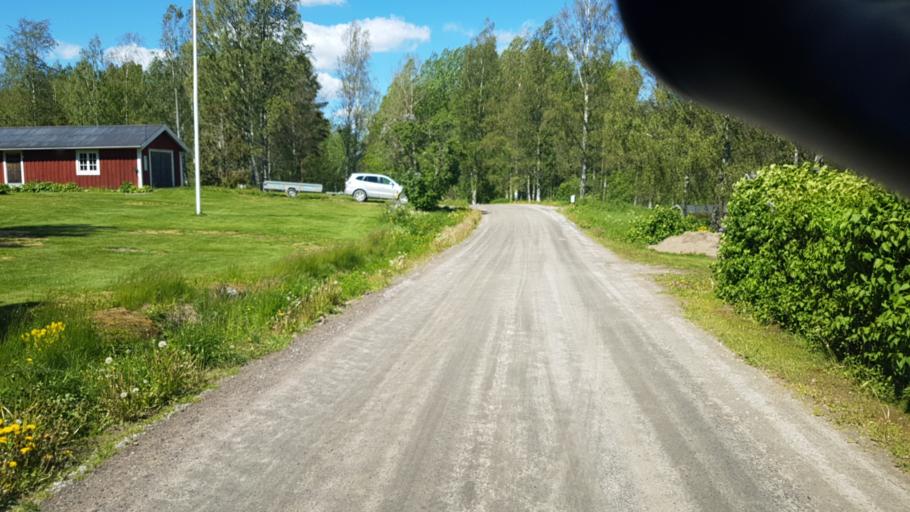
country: SE
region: Vaermland
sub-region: Arvika Kommun
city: Arvika
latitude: 59.5925
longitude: 12.8086
